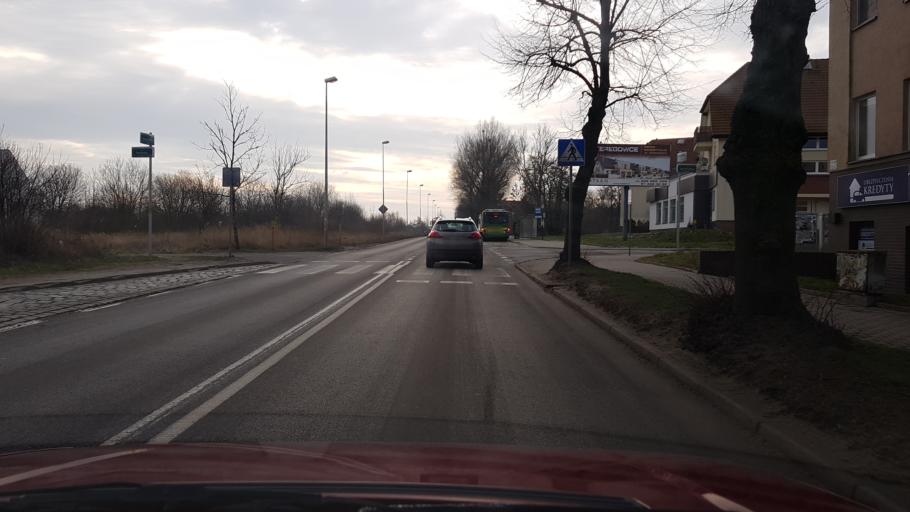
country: PL
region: West Pomeranian Voivodeship
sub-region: Powiat policki
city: Police
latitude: 53.4881
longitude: 14.5853
